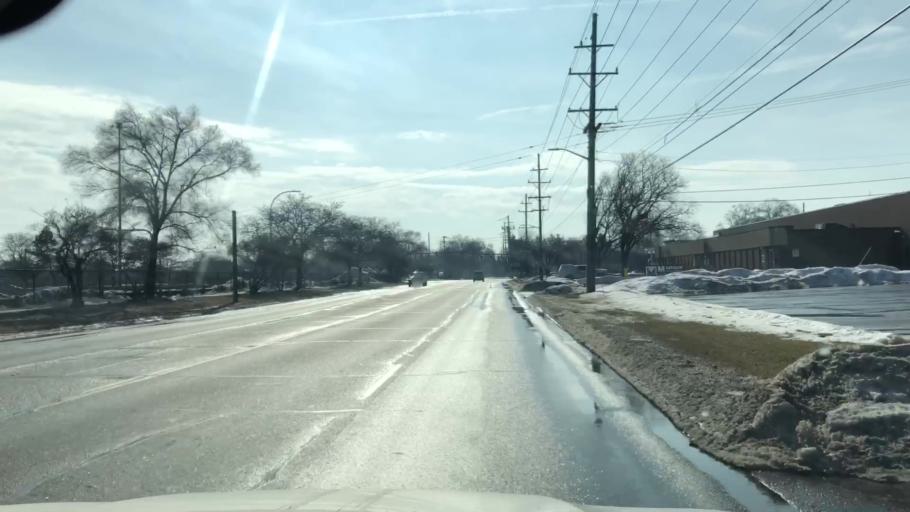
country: US
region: Michigan
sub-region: Wayne County
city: Westland
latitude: 42.3694
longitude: -83.4018
